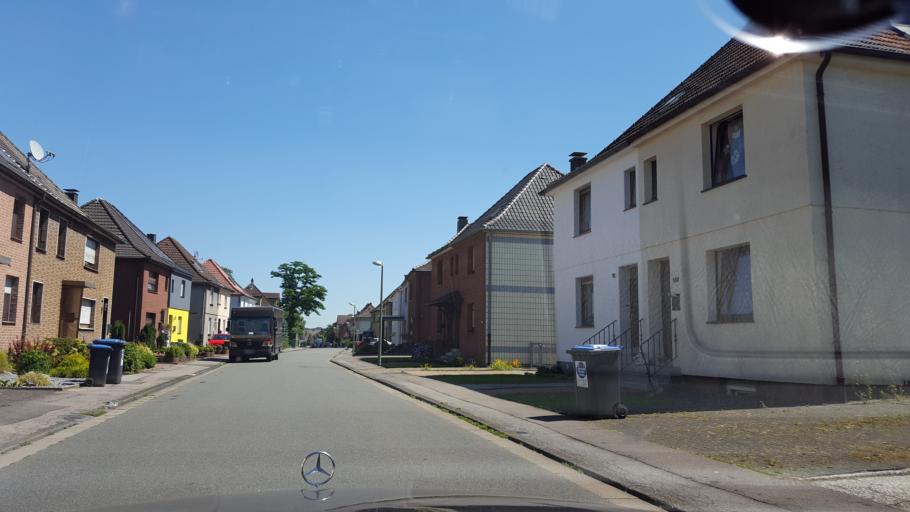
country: DE
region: North Rhine-Westphalia
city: Marl
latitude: 51.6641
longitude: 7.1419
